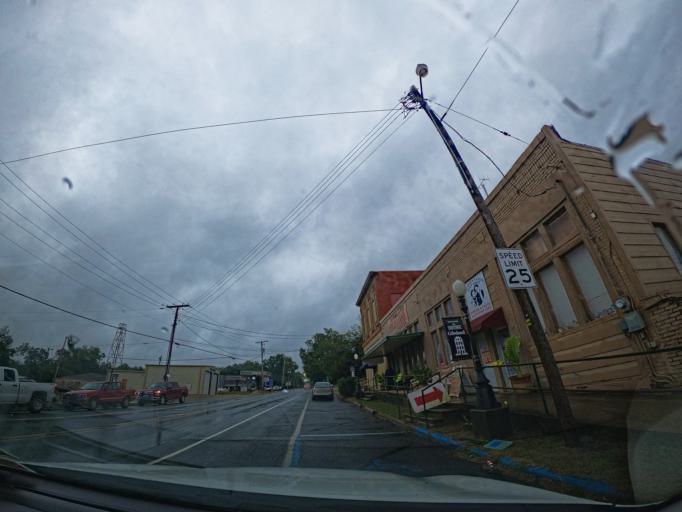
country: US
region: Louisiana
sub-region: Bienville Parish
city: Arcadia
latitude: 32.5449
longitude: -93.0531
